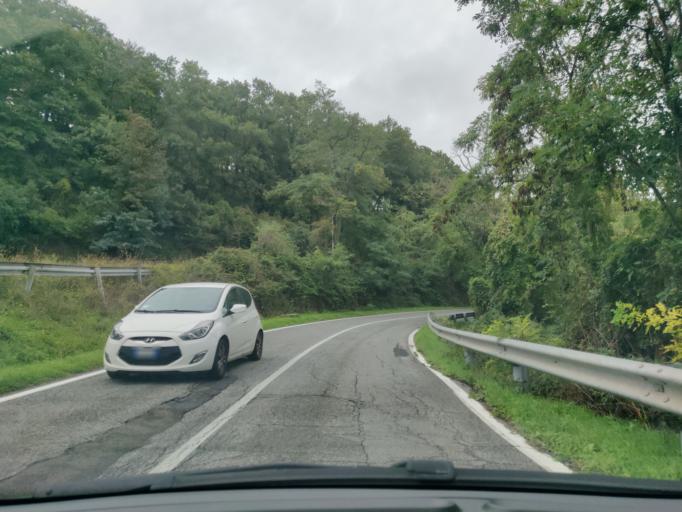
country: IT
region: Latium
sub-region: Citta metropolitana di Roma Capitale
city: Allumiere
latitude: 42.1502
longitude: 11.8991
